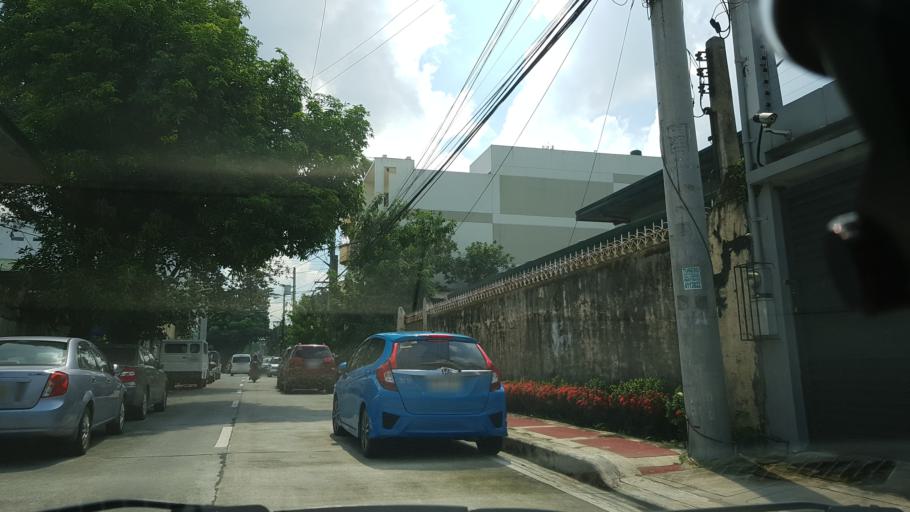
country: PH
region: Calabarzon
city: Del Monte
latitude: 14.6317
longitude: 121.0244
